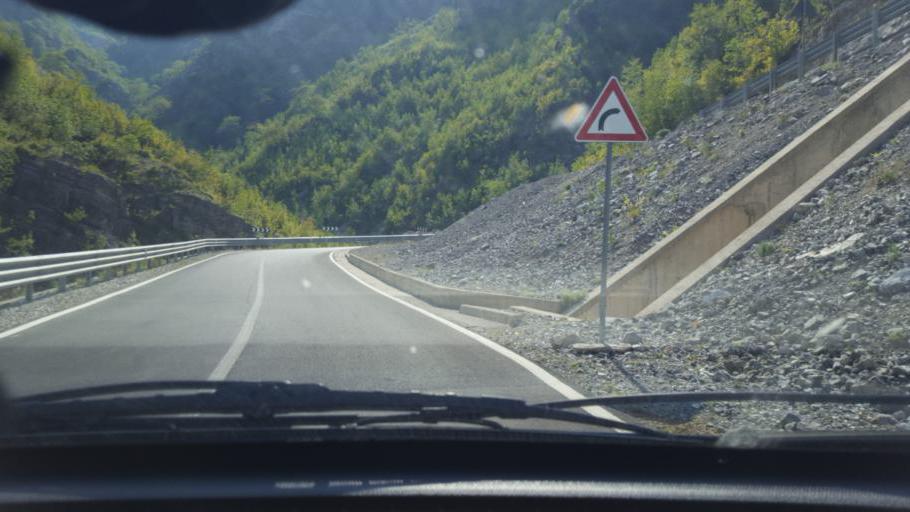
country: AL
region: Shkoder
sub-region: Rrethi i Malesia e Madhe
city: Kastrat
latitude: 42.4130
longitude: 19.5103
